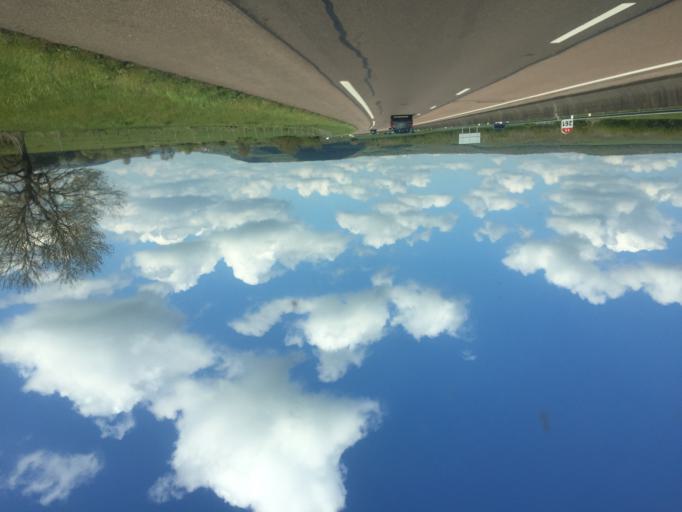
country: FR
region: Bourgogne
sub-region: Departement de la Cote-d'Or
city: Pouilly-en-Auxois
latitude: 47.2652
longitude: 4.5176
